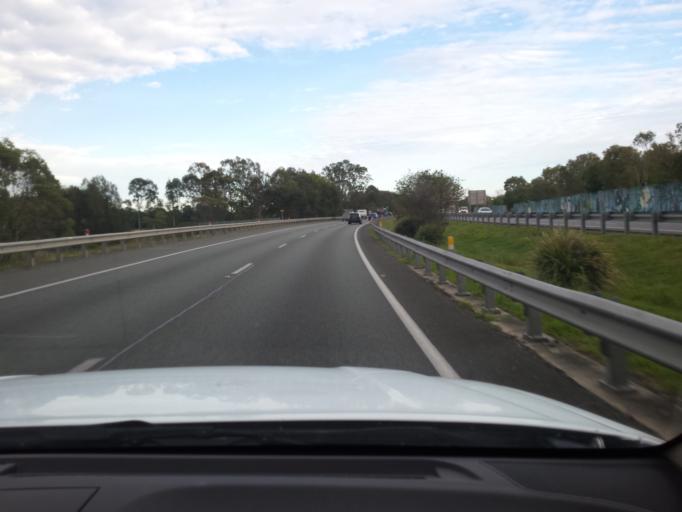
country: AU
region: Queensland
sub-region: Logan
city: Slacks Creek
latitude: -27.6828
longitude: 153.1724
